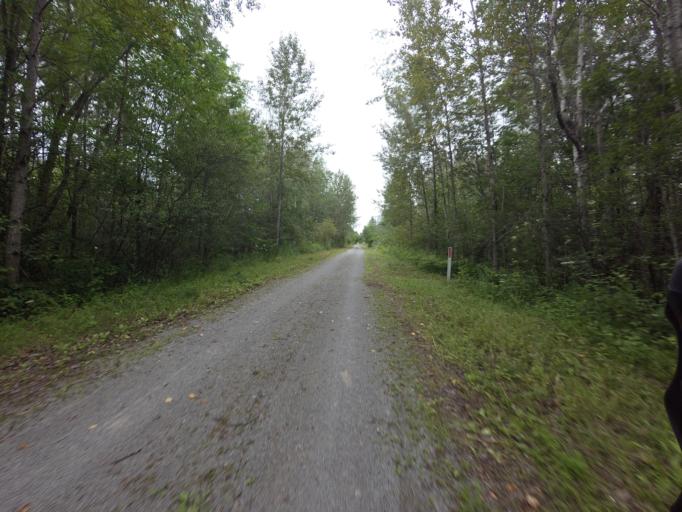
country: CA
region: Ontario
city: Ottawa
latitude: 45.2667
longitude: -75.6236
